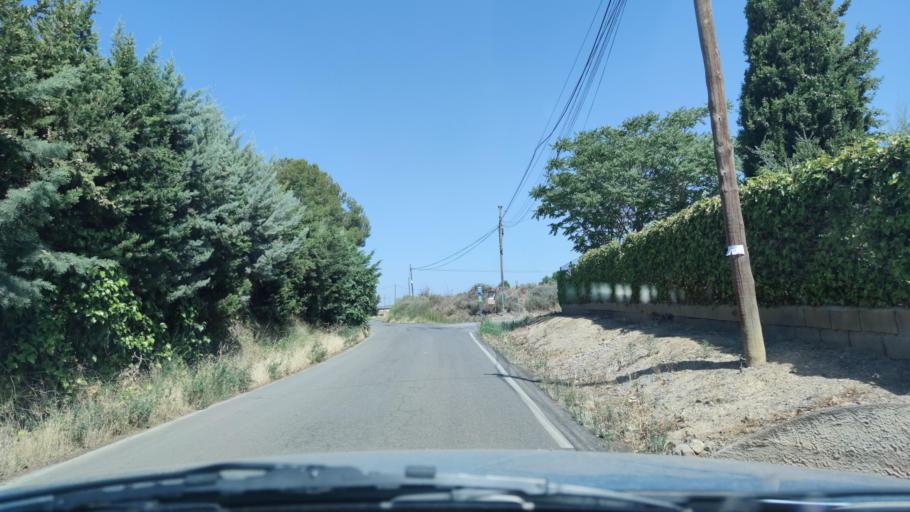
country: ES
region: Catalonia
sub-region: Provincia de Lleida
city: Alpicat
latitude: 41.6481
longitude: 0.5828
